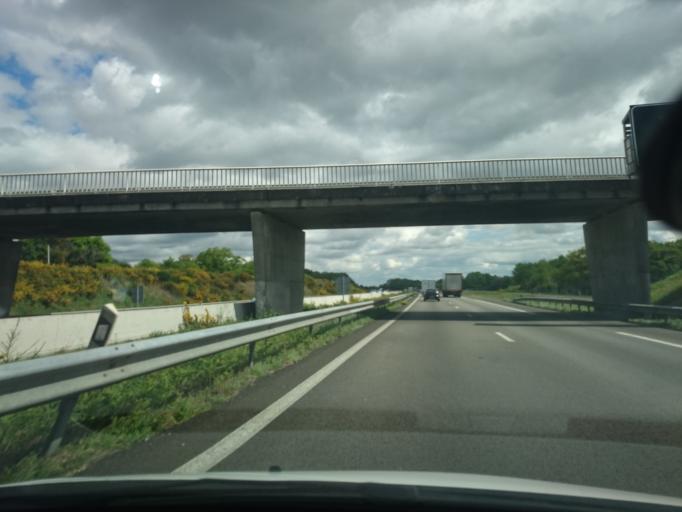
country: FR
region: Pays de la Loire
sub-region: Departement de la Loire-Atlantique
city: Sautron
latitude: 47.2624
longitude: -1.7035
